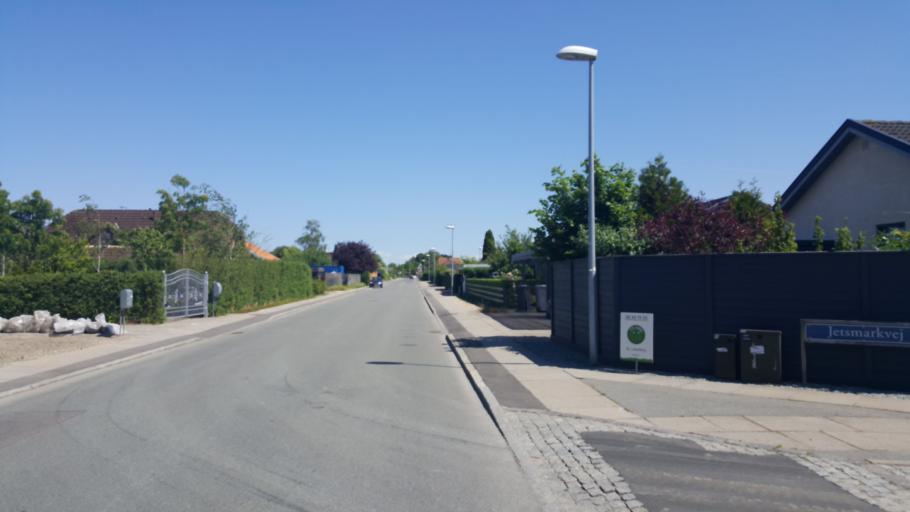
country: DK
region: Capital Region
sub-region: Tarnby Kommune
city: Tarnby
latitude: 55.6176
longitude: 12.6003
